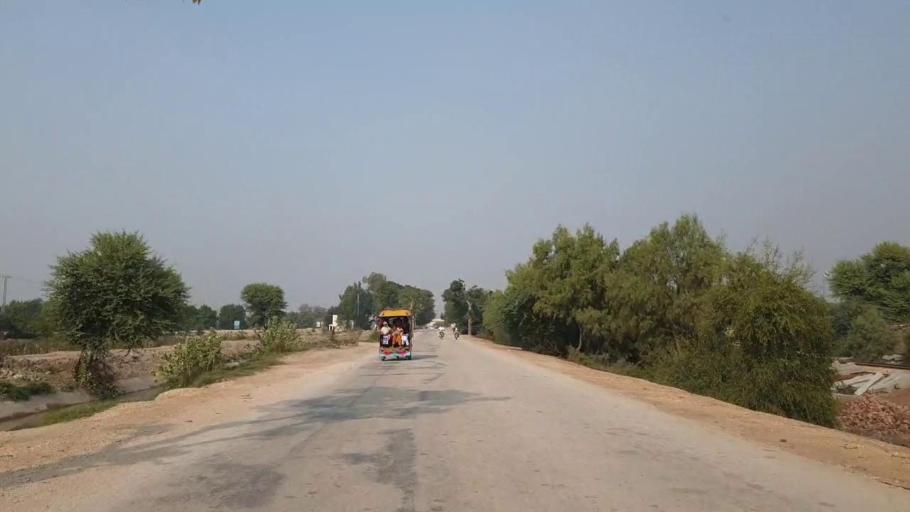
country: PK
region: Sindh
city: Bhan
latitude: 26.5849
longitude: 67.7290
